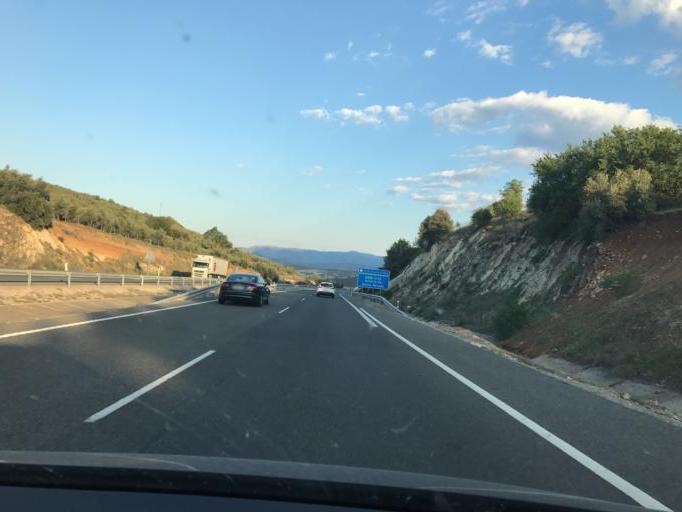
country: ES
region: Andalusia
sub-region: Provincia de Granada
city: Campotejar
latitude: 37.4664
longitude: -3.5676
